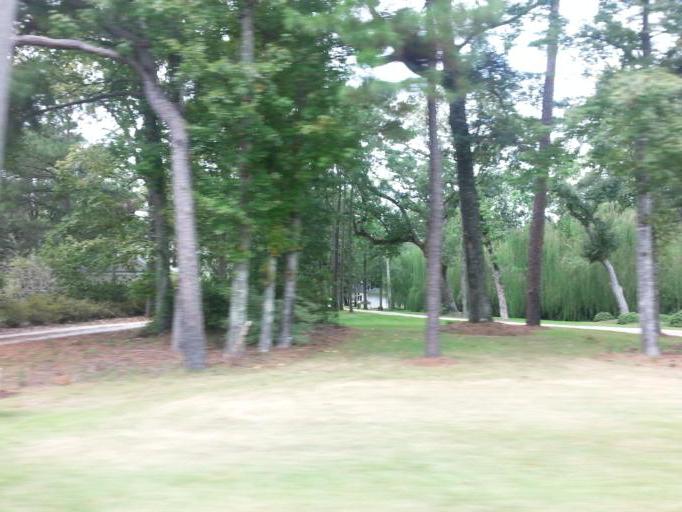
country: US
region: Alabama
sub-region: Baldwin County
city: Fairhope
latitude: 30.5036
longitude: -87.9221
